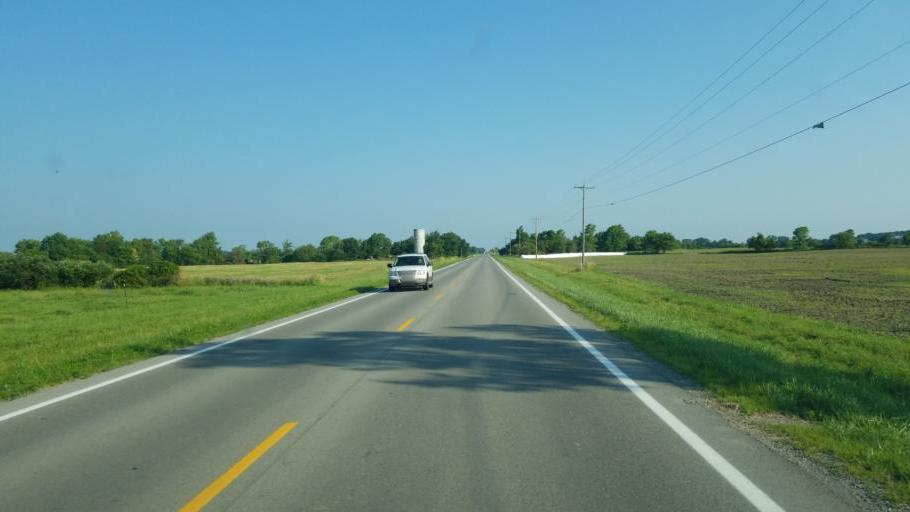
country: US
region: Ohio
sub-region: Hardin County
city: Kenton
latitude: 40.5549
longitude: -83.5380
